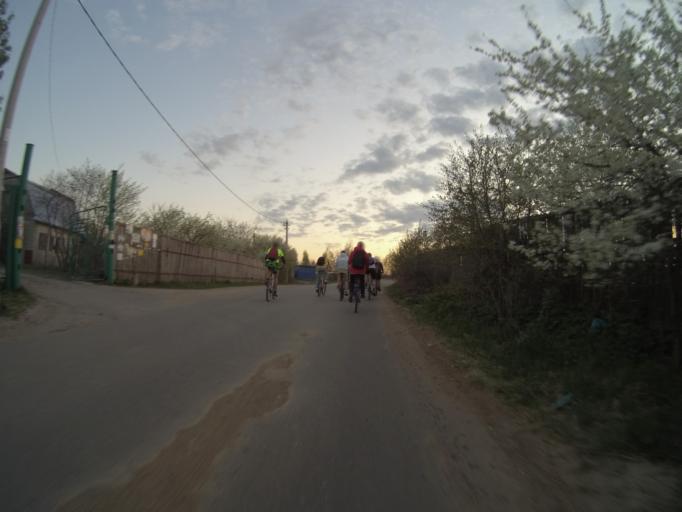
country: RU
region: Vladimir
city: Vladimir
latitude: 56.1382
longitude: 40.3289
